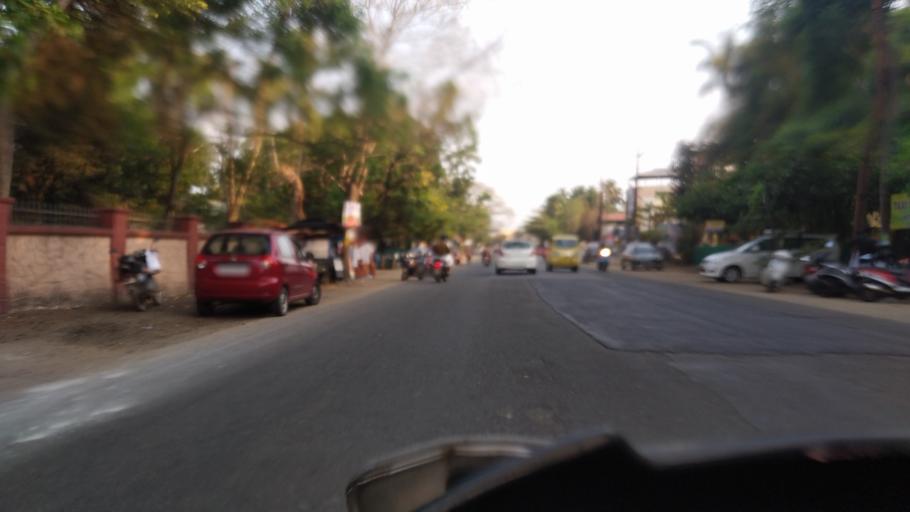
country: IN
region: Kerala
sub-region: Thrissur District
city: Thanniyam
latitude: 10.4192
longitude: 76.1054
